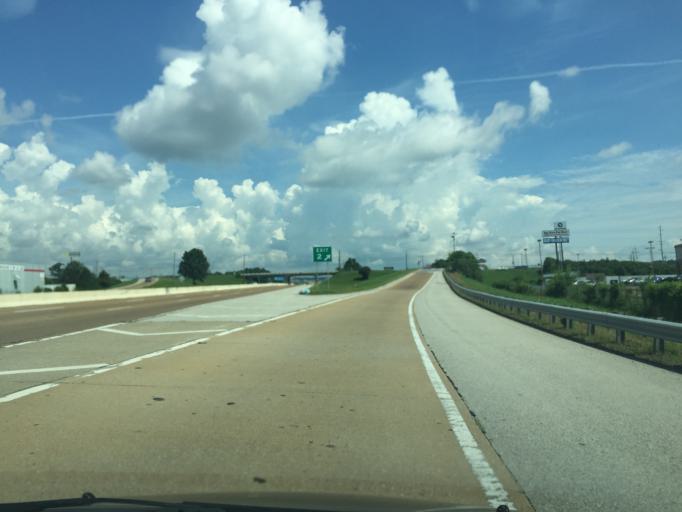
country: US
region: Tennessee
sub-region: Hamilton County
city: East Chattanooga
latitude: 35.0515
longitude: -85.1896
